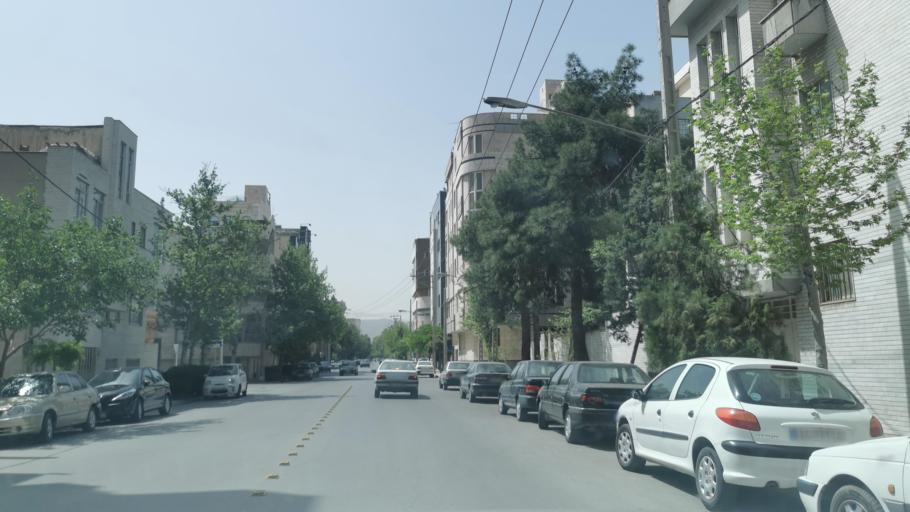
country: IR
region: Razavi Khorasan
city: Mashhad
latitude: 36.3078
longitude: 59.5599
